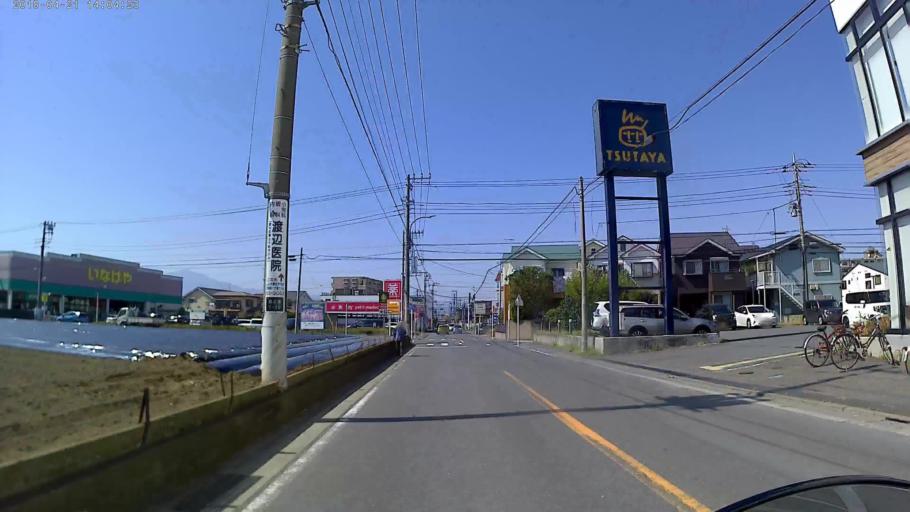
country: JP
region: Kanagawa
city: Hiratsuka
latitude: 35.3503
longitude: 139.3512
